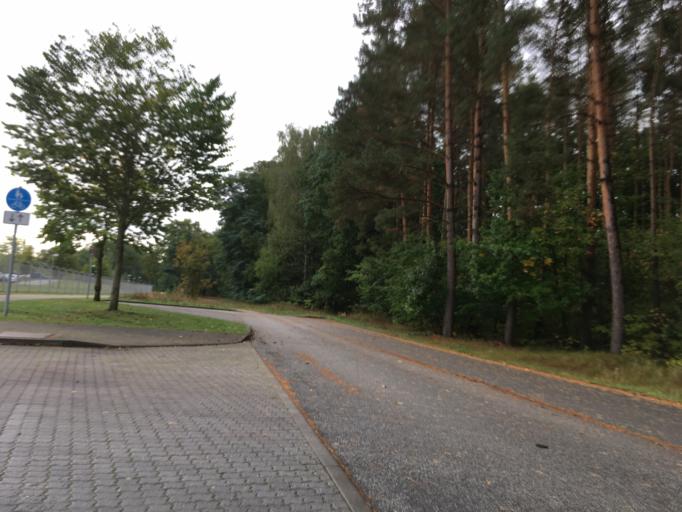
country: DE
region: Brandenburg
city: Ahrensfelde
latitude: 52.5977
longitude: 13.5765
